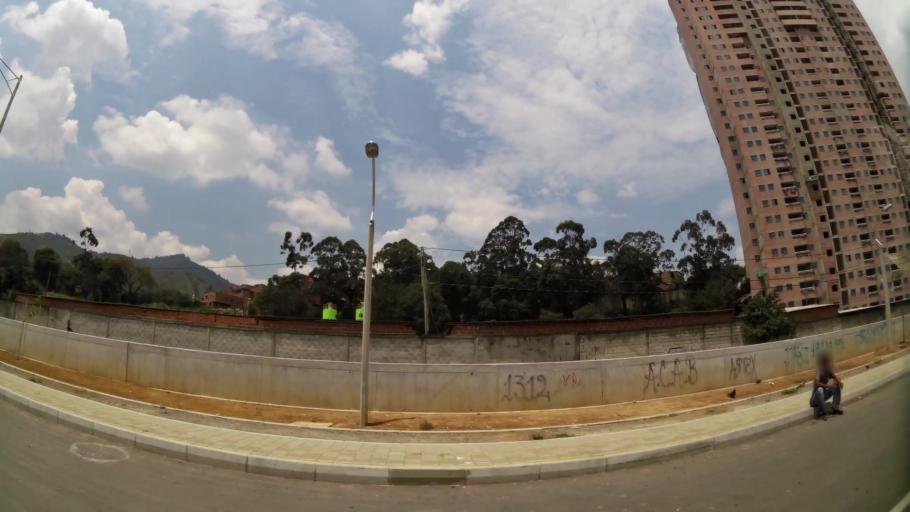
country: CO
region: Antioquia
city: Itagui
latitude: 6.1760
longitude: -75.6084
